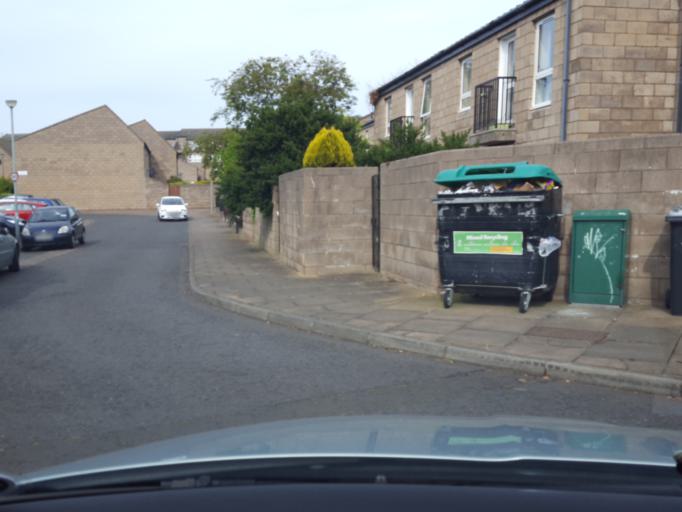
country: GB
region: Scotland
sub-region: Edinburgh
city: Edinburgh
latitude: 55.9730
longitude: -3.1794
